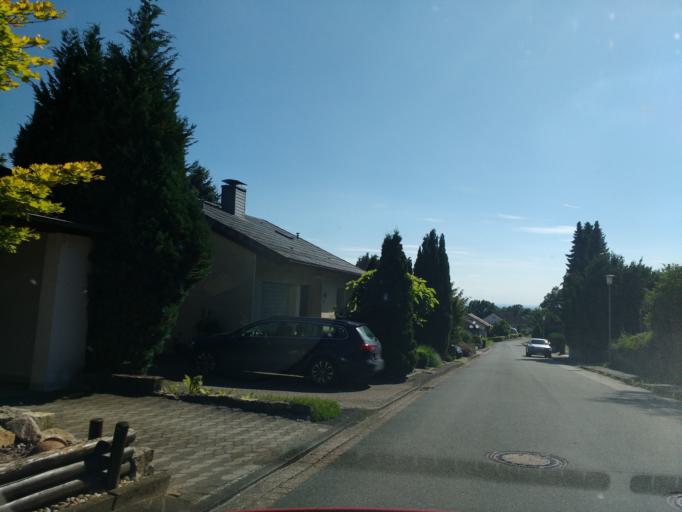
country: DE
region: North Rhine-Westphalia
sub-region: Regierungsbezirk Detmold
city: Schlangen
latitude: 51.8293
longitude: 8.8641
